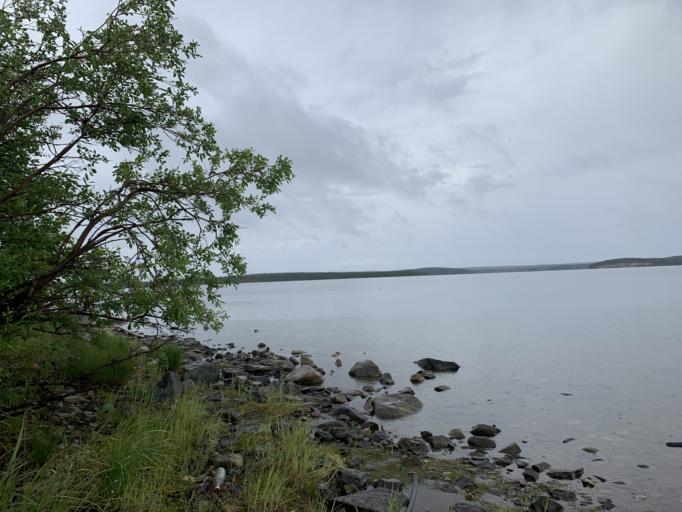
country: RU
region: Murmansk
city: Monchegorsk
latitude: 67.9374
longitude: 32.9918
